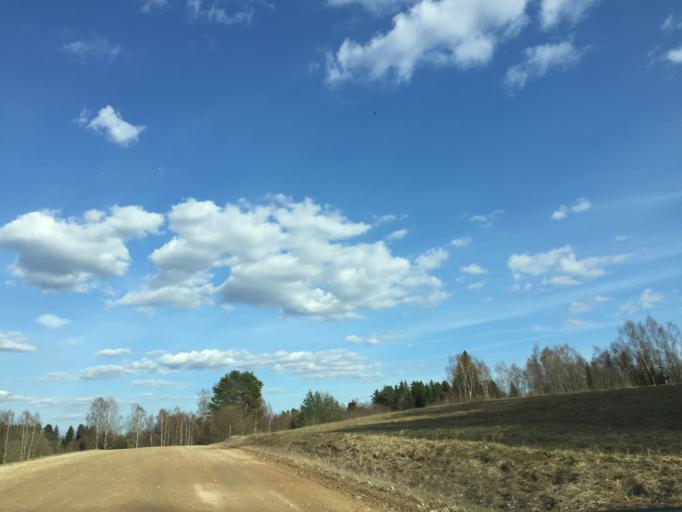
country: EE
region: Tartu
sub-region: Noo vald
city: Noo
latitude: 58.1119
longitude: 26.5448
